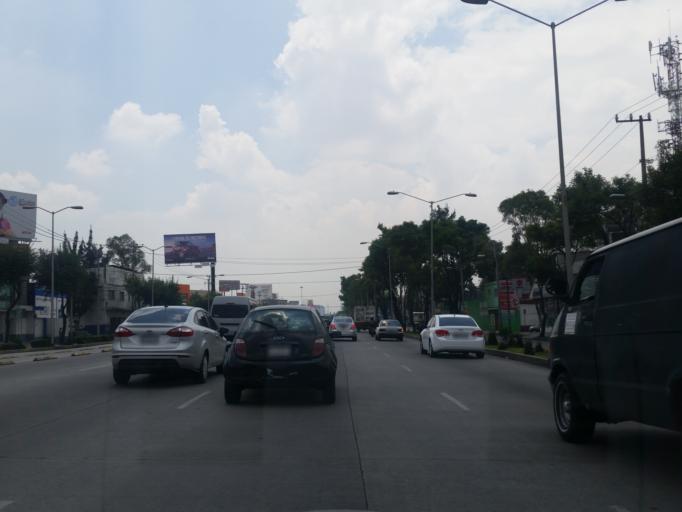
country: MX
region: Mexico
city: Colonia Lindavista
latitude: 19.4783
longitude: -99.1479
